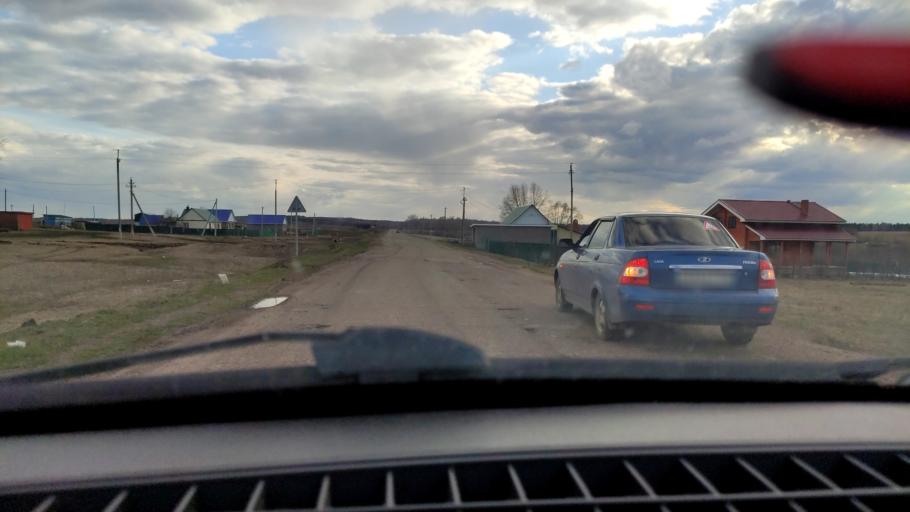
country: RU
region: Bashkortostan
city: Karmaskaly
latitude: 54.3324
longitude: 55.9939
